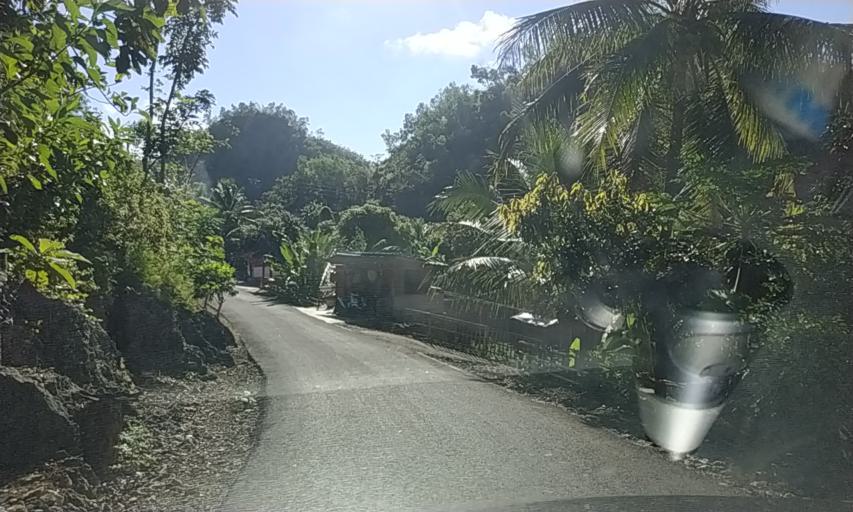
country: ID
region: East Java
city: Krajan
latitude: -8.1284
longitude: 110.8959
